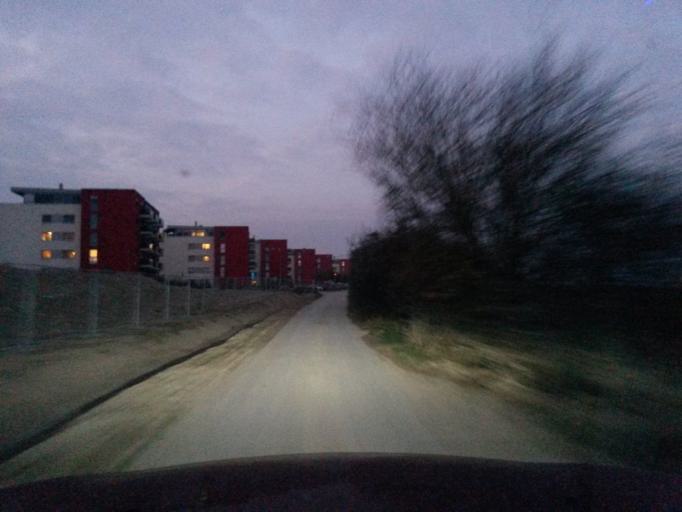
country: SK
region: Kosicky
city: Kosice
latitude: 48.7181
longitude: 21.2939
